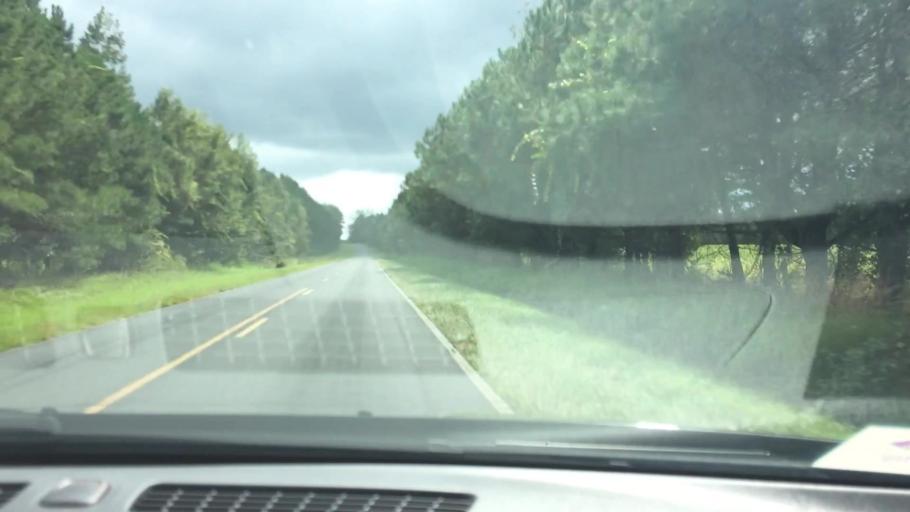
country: US
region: North Carolina
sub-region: Greene County
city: Maury
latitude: 35.5300
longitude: -77.5447
